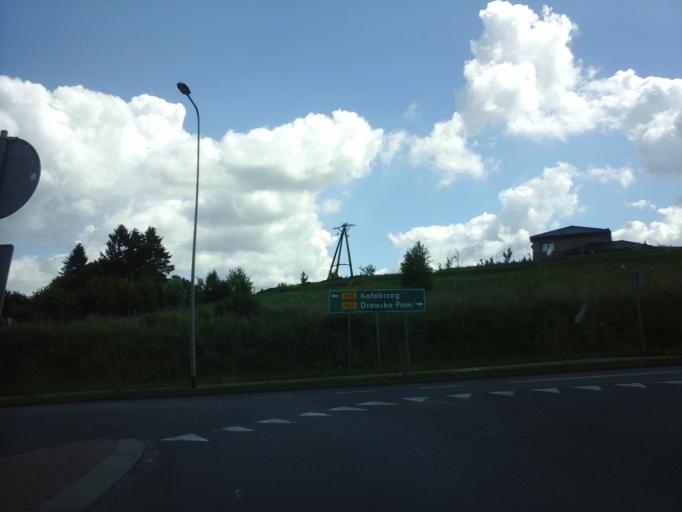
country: PL
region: West Pomeranian Voivodeship
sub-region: Powiat swidwinski
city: Swidwin
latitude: 53.7872
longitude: 15.7791
